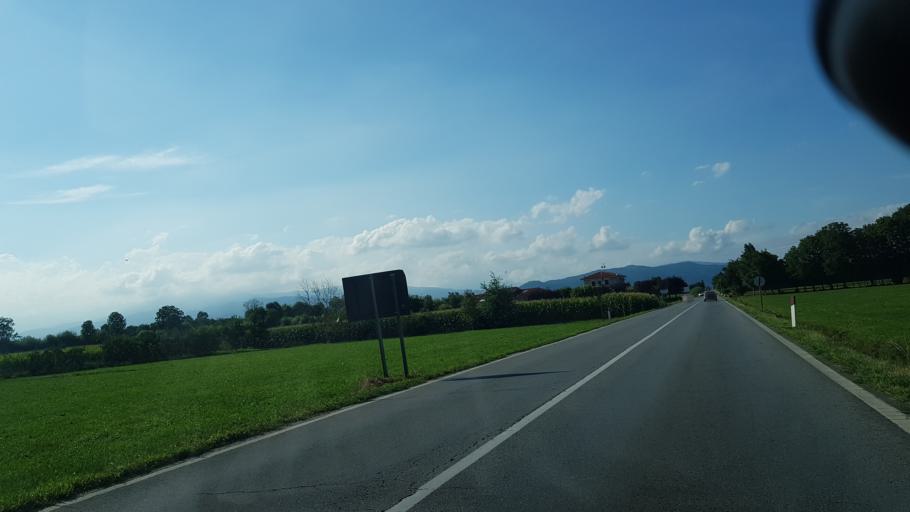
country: IT
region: Piedmont
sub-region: Provincia di Cuneo
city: Roata Rossi
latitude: 44.4496
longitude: 7.5260
